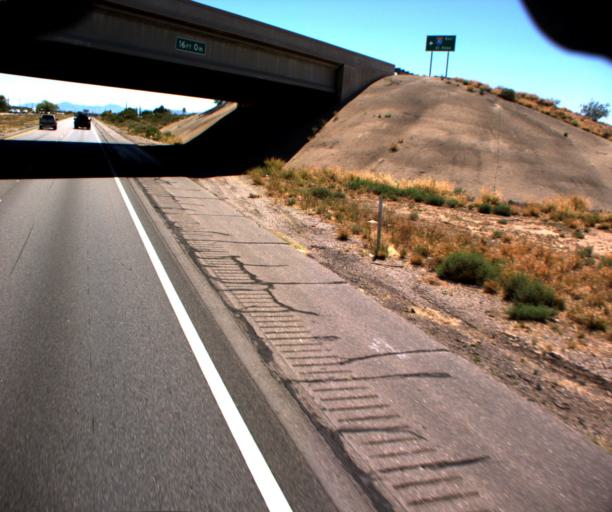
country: US
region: Arizona
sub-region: Pima County
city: Summit
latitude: 32.1039
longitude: -110.8414
